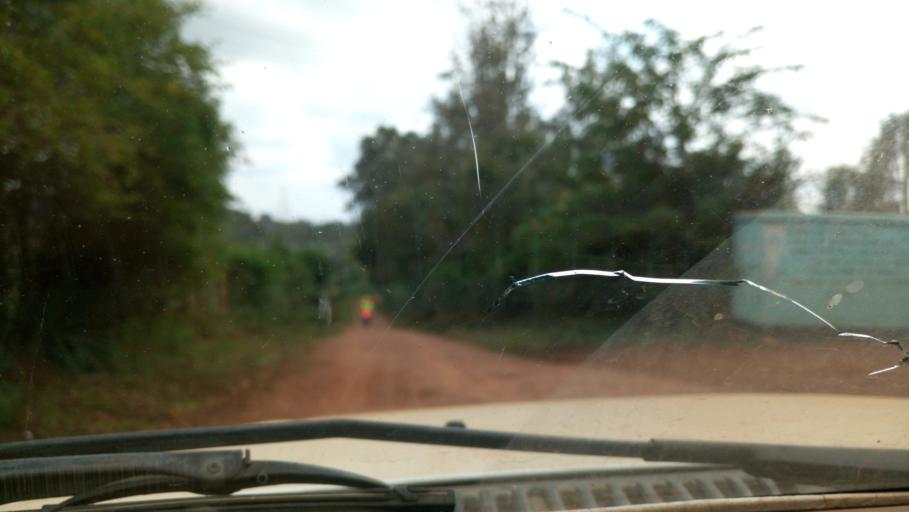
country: KE
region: Murang'a District
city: Maragua
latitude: -0.8510
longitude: 37.0527
